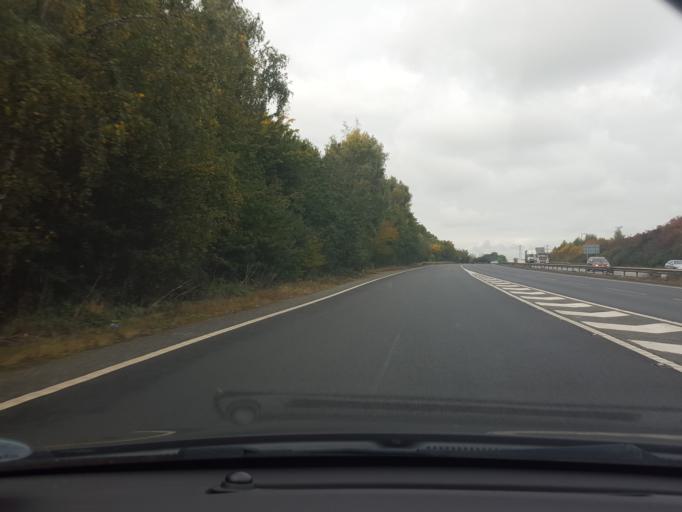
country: GB
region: England
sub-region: Suffolk
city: Bramford
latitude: 52.0386
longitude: 1.0961
